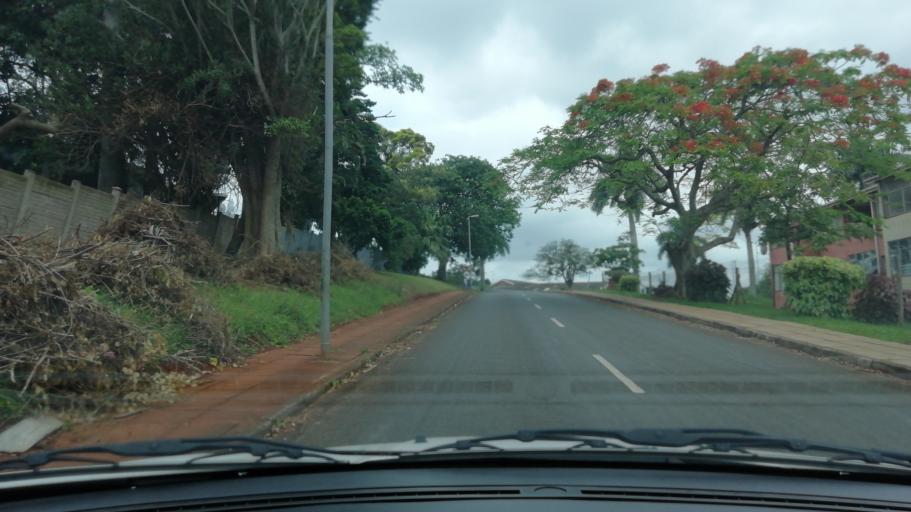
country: ZA
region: KwaZulu-Natal
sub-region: uThungulu District Municipality
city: Empangeni
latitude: -28.7546
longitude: 31.8933
